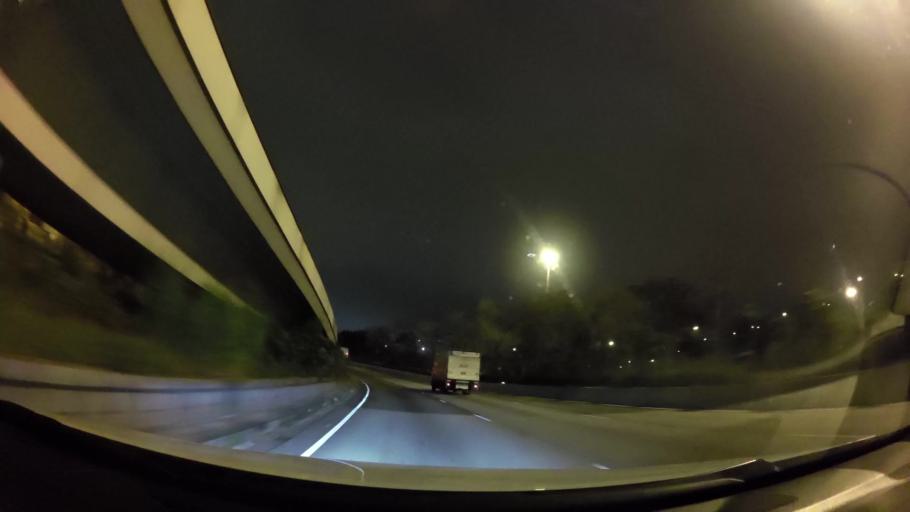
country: HK
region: Sham Shui Po
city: Sham Shui Po
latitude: 22.3390
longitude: 114.1330
